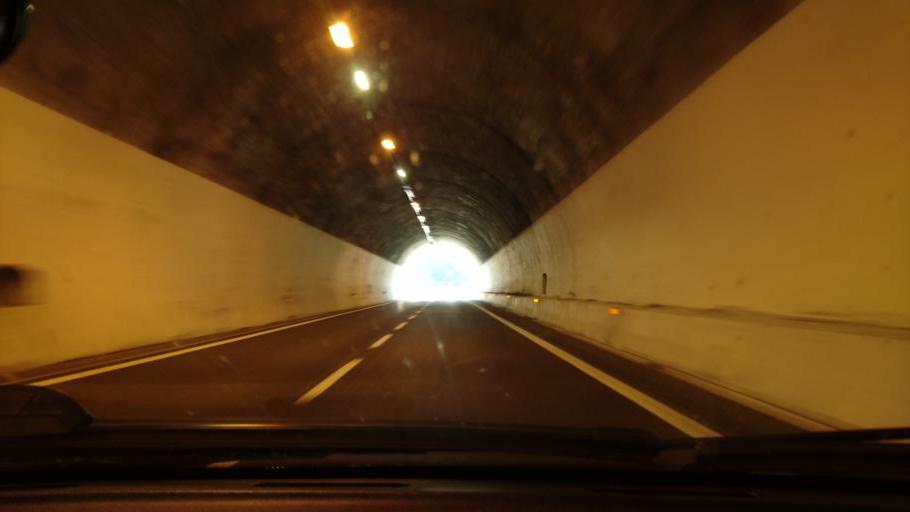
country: IT
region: Liguria
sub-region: Provincia di Savona
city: Altare
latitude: 44.3225
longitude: 8.3612
